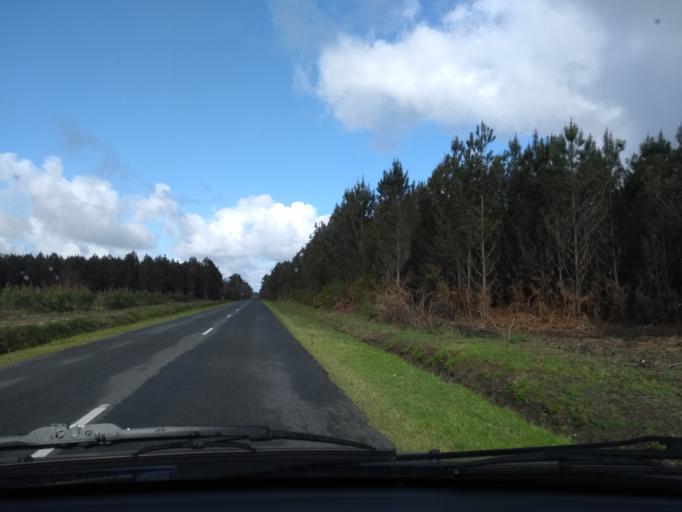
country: FR
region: Aquitaine
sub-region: Departement de la Gironde
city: Mios
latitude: 44.5510
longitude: -0.9495
